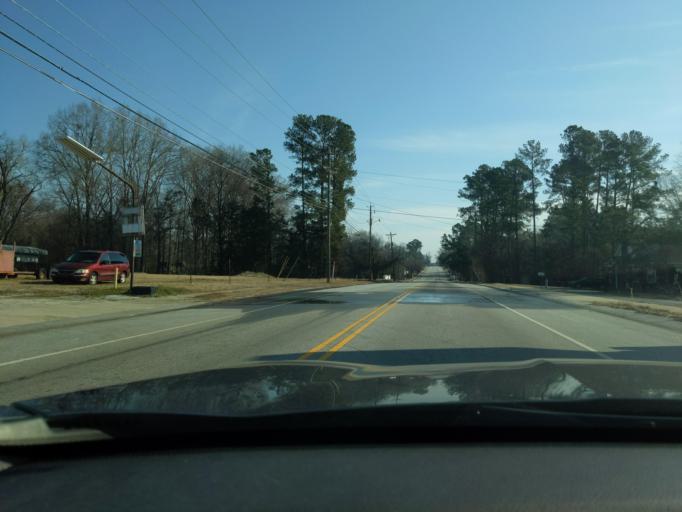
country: US
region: South Carolina
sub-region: Abbeville County
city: Calhoun Falls
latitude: 34.0906
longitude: -82.5849
